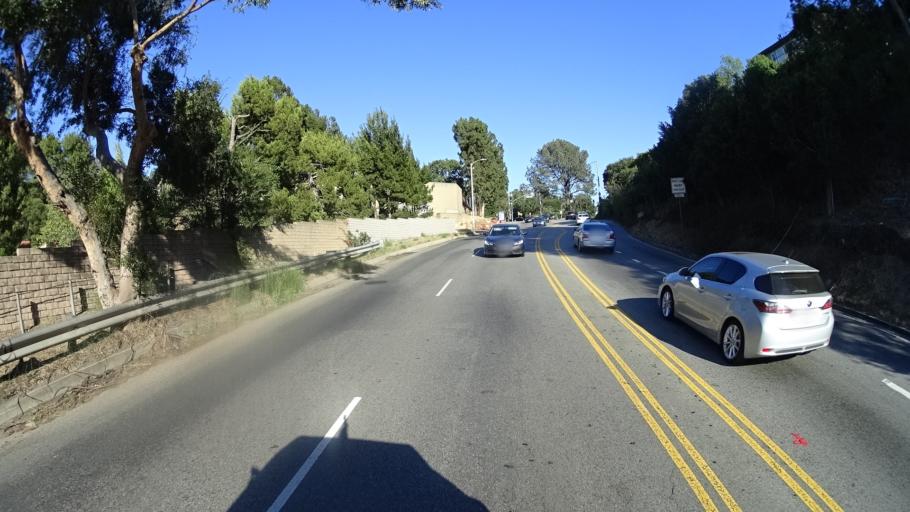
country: US
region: California
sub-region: Los Angeles County
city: Universal City
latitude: 34.1243
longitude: -118.3762
